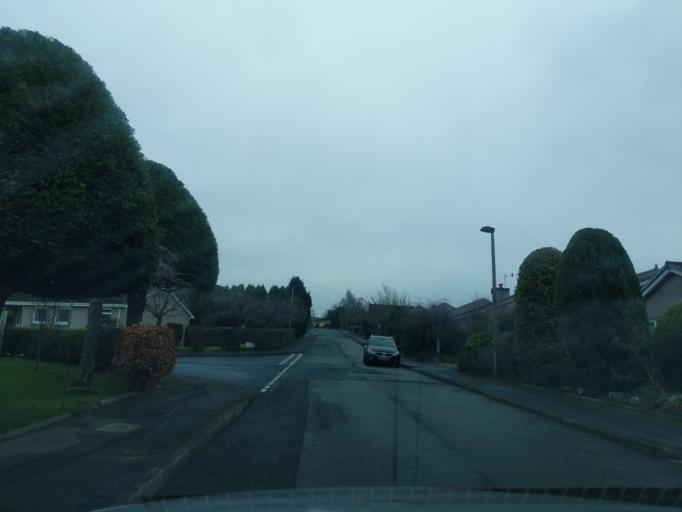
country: GB
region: Scotland
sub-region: Edinburgh
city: Balerno
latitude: 55.8930
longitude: -3.3291
